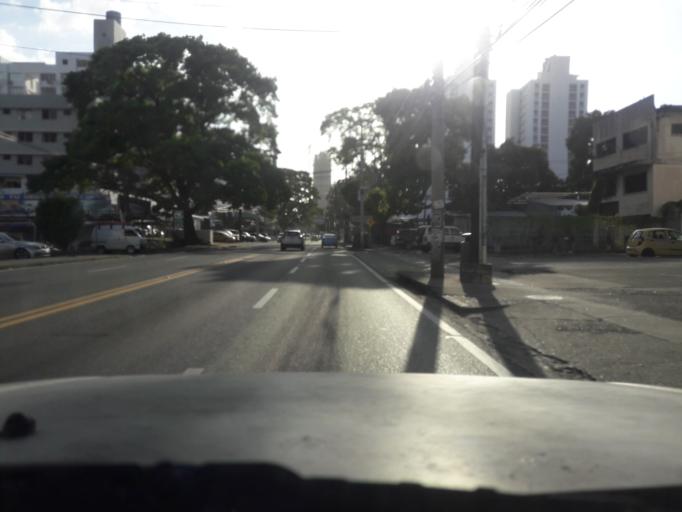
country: PA
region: Panama
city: Panama
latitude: 9.0110
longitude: -79.5043
